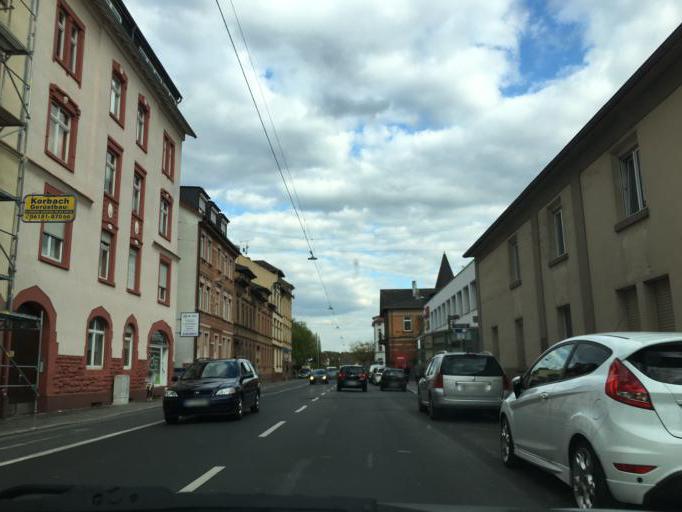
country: DE
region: Hesse
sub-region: Regierungsbezirk Darmstadt
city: Offenbach
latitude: 50.1016
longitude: 8.7782
